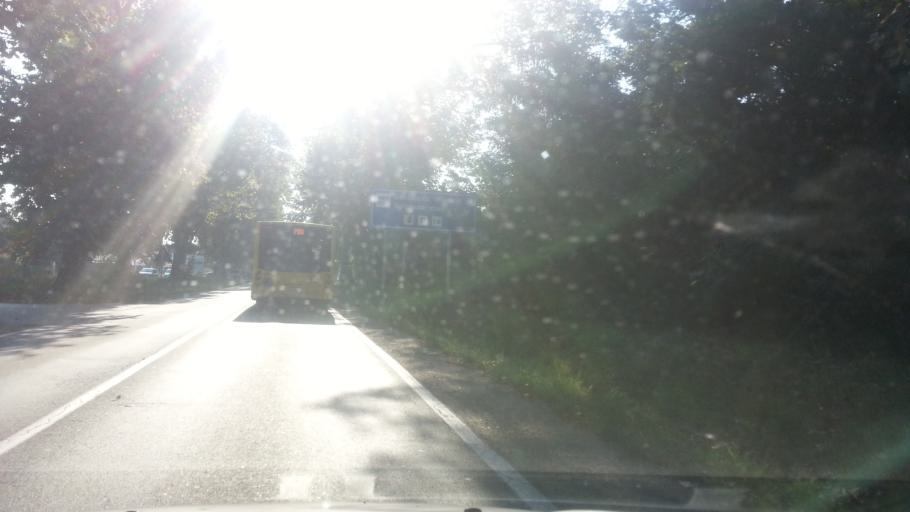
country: RS
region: Central Serbia
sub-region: Belgrade
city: Zemun
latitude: 44.8694
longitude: 20.3540
